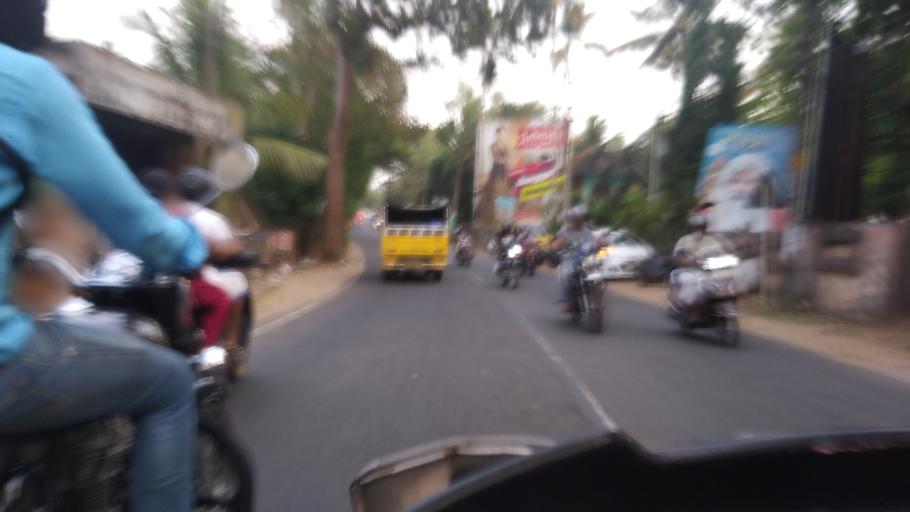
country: IN
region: Kerala
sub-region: Thrissur District
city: Kodungallur
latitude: 10.2433
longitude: 76.1907
